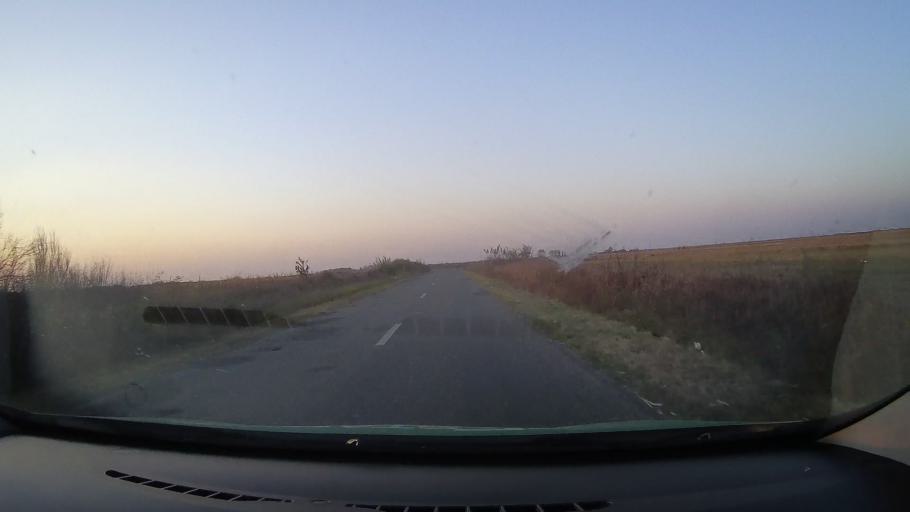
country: RO
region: Arad
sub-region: Comuna Zarand
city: Zarand
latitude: 46.3870
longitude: 21.6634
